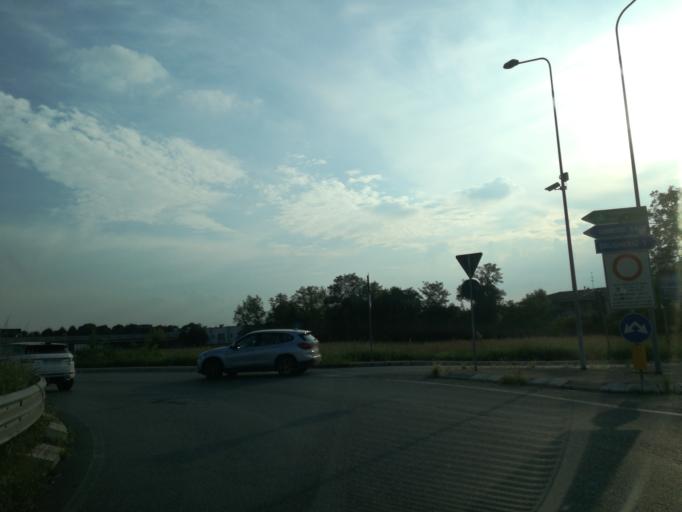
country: IT
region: Lombardy
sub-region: Citta metropolitana di Milano
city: Carugate
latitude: 45.5537
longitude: 9.3327
